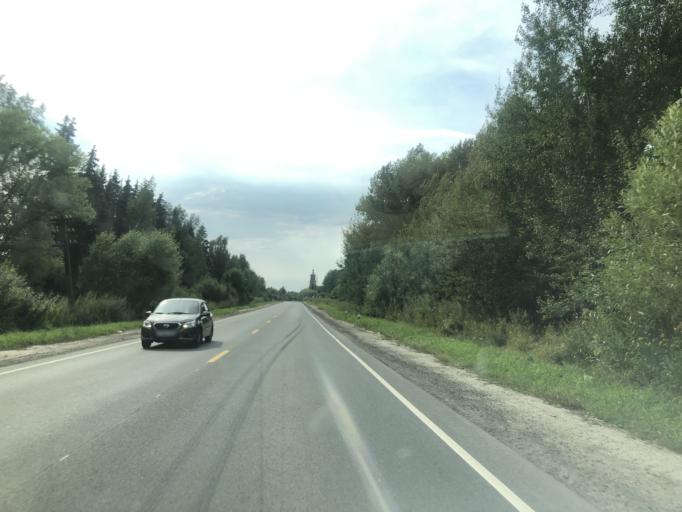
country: RU
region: Ivanovo
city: Shuya
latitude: 56.8534
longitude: 41.5609
